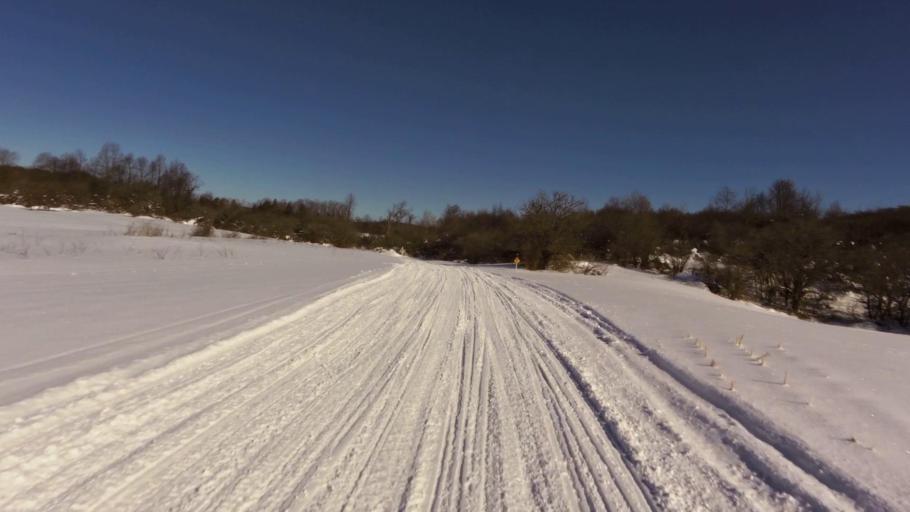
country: US
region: New York
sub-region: Cattaraugus County
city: Franklinville
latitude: 42.3990
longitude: -78.4955
